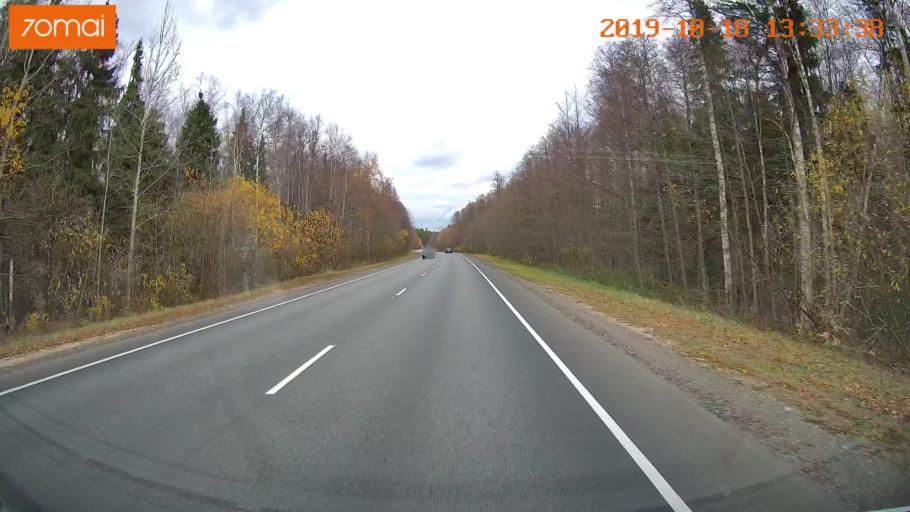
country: RU
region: Rjazan
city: Solotcha
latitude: 54.8455
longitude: 39.9400
